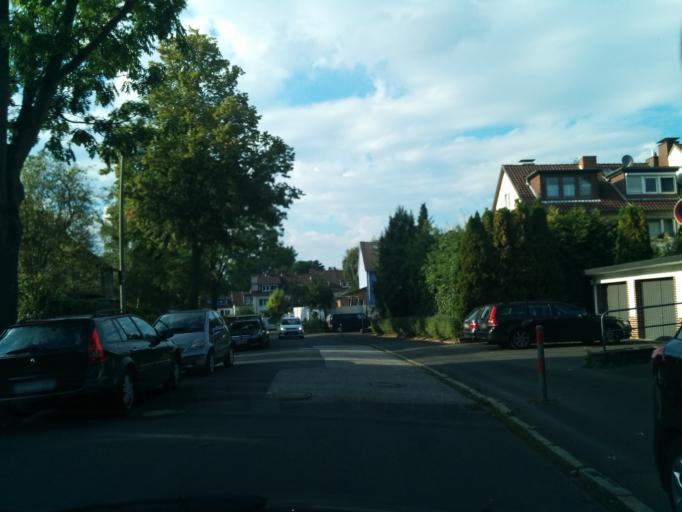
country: DE
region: Lower Saxony
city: Goettingen
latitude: 51.5407
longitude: 9.9563
